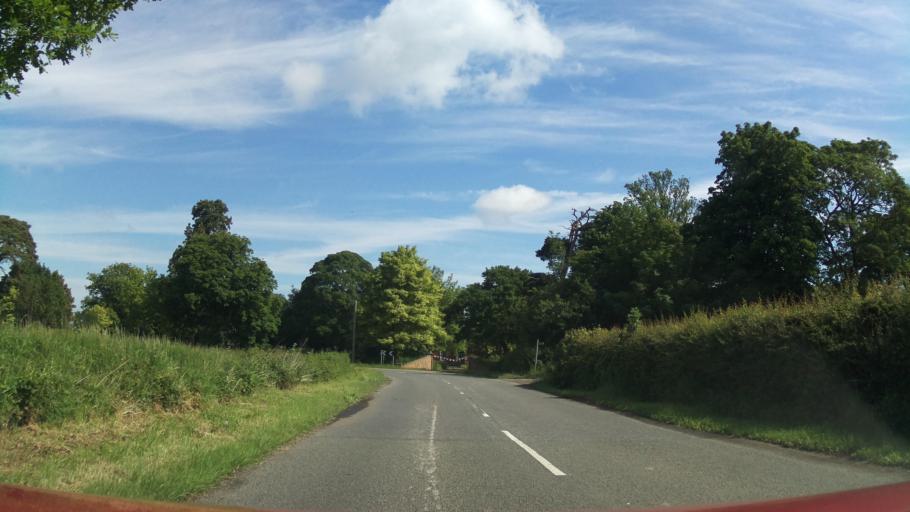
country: GB
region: England
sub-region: Lincolnshire
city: Skellingthorpe
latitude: 53.1374
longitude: -0.6326
